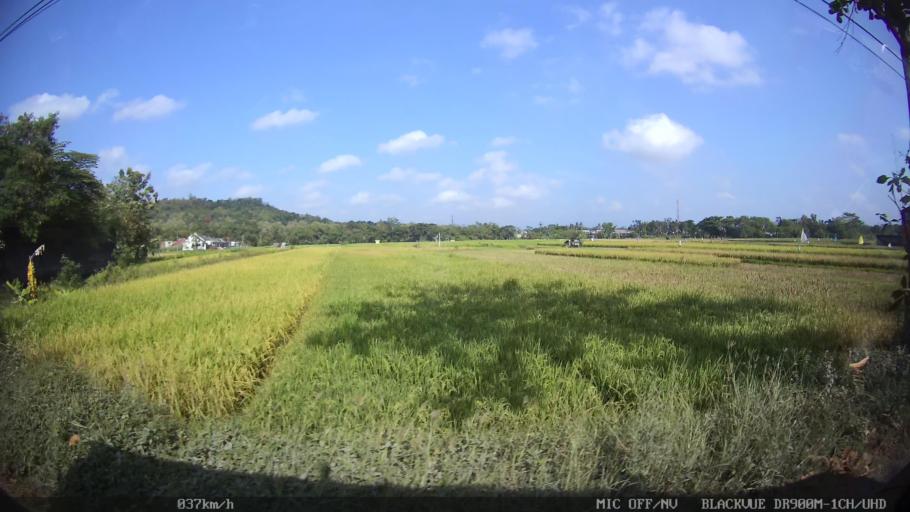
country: ID
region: Daerah Istimewa Yogyakarta
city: Gamping Lor
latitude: -7.8079
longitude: 110.2991
